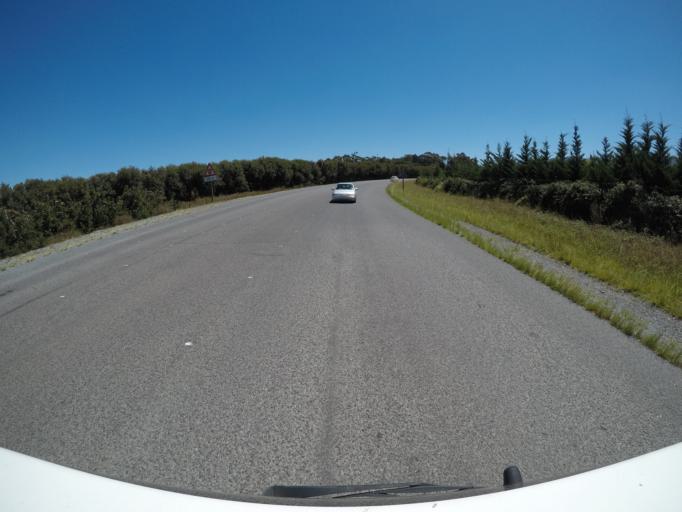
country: ZA
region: Western Cape
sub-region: Overberg District Municipality
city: Grabouw
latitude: -34.1673
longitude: 19.0363
